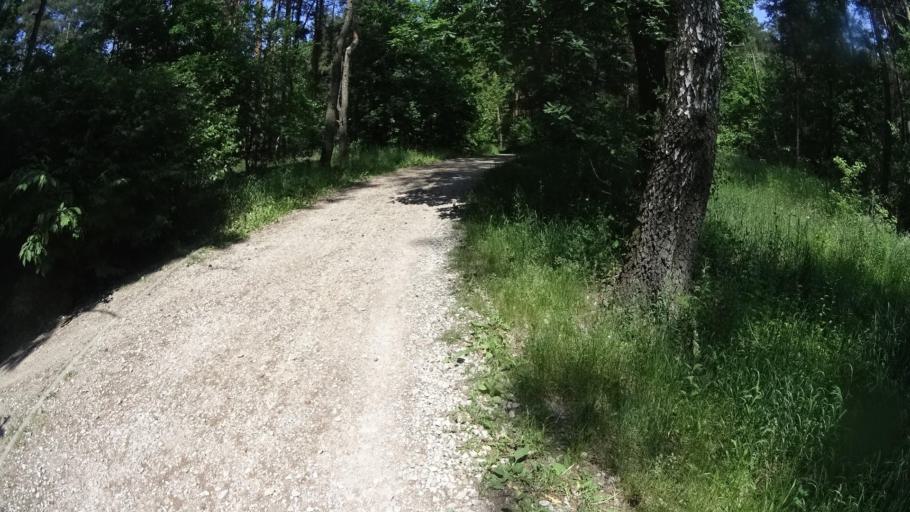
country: PL
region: Masovian Voivodeship
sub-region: Powiat warszawski zachodni
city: Stare Babice
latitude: 52.2713
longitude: 20.8416
